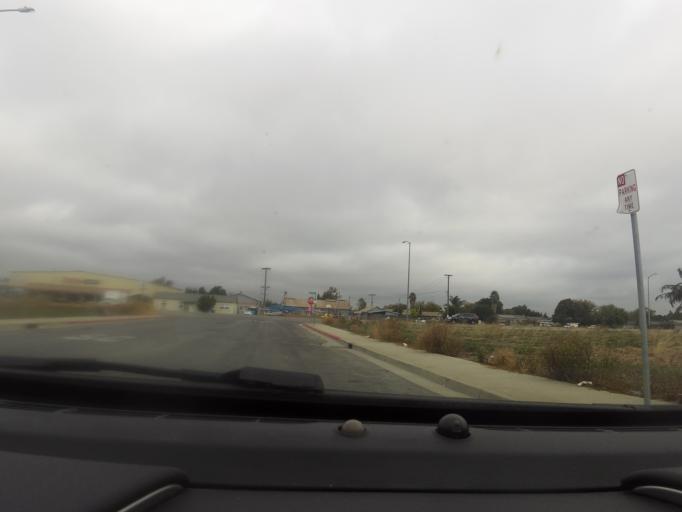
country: US
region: California
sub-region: San Benito County
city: Hollister
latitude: 36.8524
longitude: -121.4188
